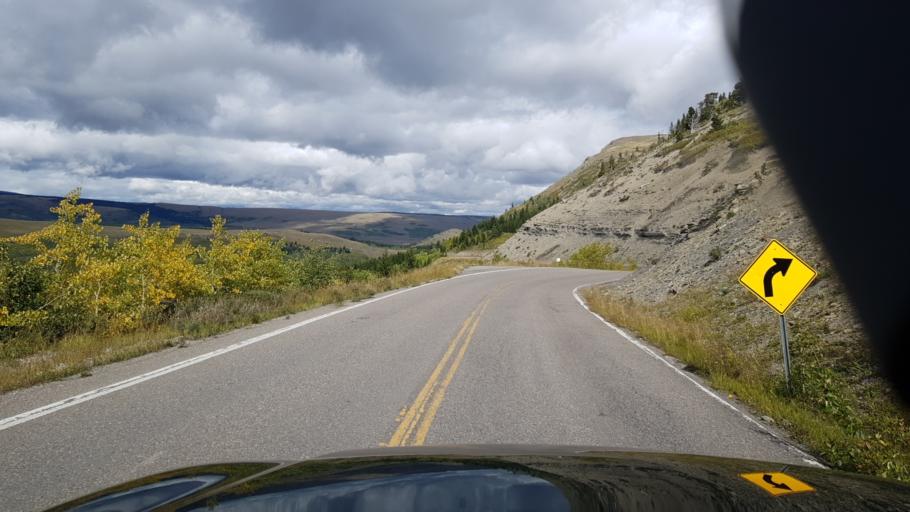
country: US
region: Montana
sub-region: Glacier County
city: South Browning
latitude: 48.5322
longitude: -113.3076
